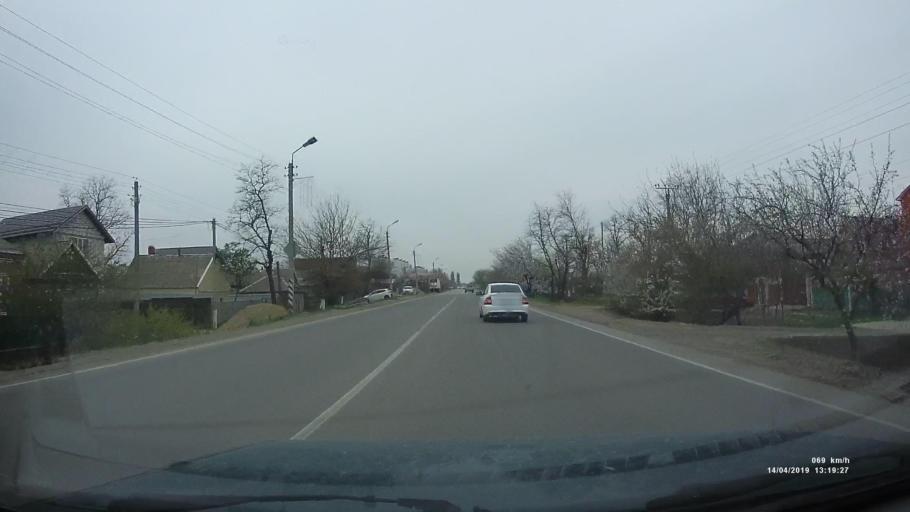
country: RU
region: Rostov
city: Kuleshovka
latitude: 47.0807
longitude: 39.5450
